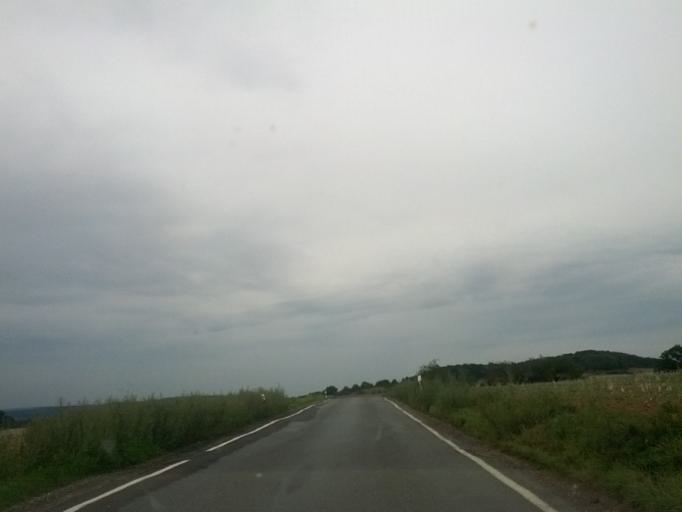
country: DE
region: Thuringia
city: Bad Salzungen
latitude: 50.8682
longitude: 10.2419
